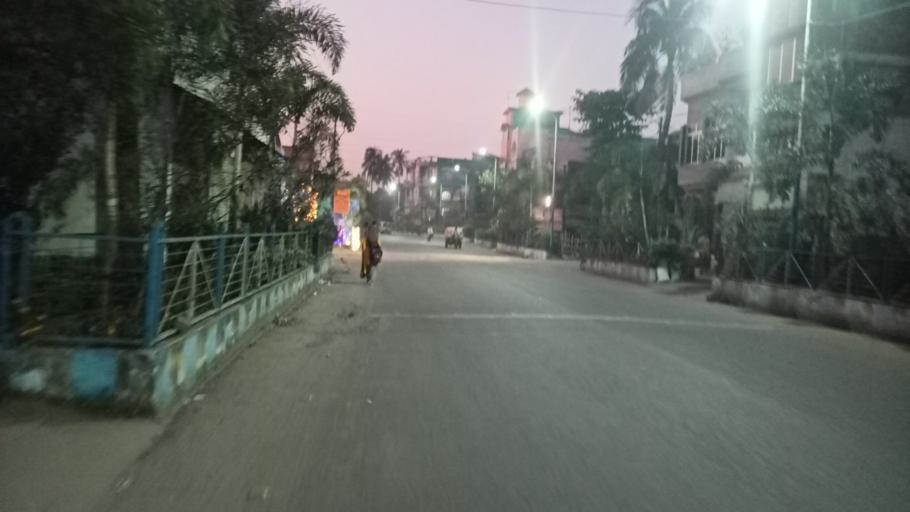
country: IN
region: West Bengal
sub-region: North 24 Parganas
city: Bangaon
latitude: 23.0475
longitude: 88.8368
